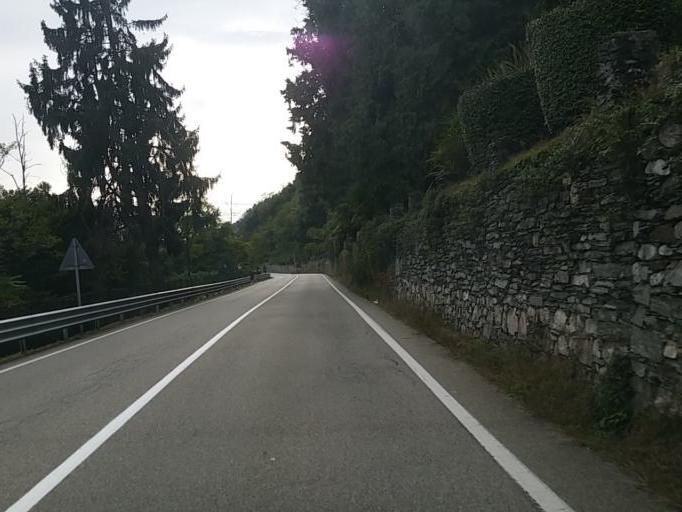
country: IT
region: Piedmont
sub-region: Provincia Verbano-Cusio-Ossola
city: Oggebbio
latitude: 45.9827
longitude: 8.6401
